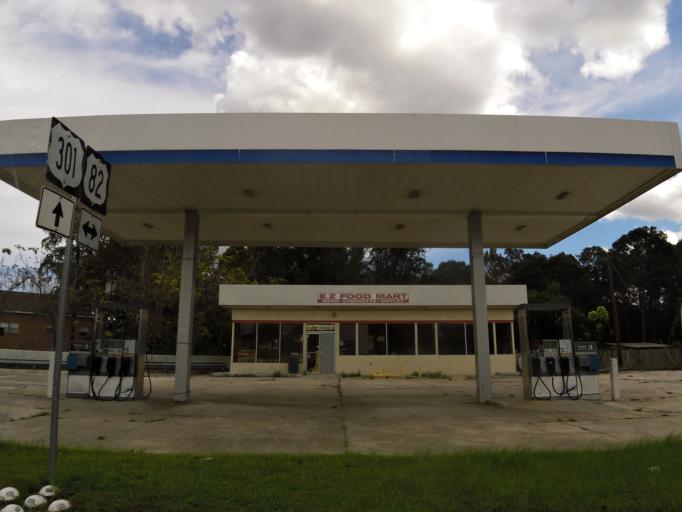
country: US
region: Georgia
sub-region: Brantley County
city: Nahunta
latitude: 31.2019
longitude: -81.9825
